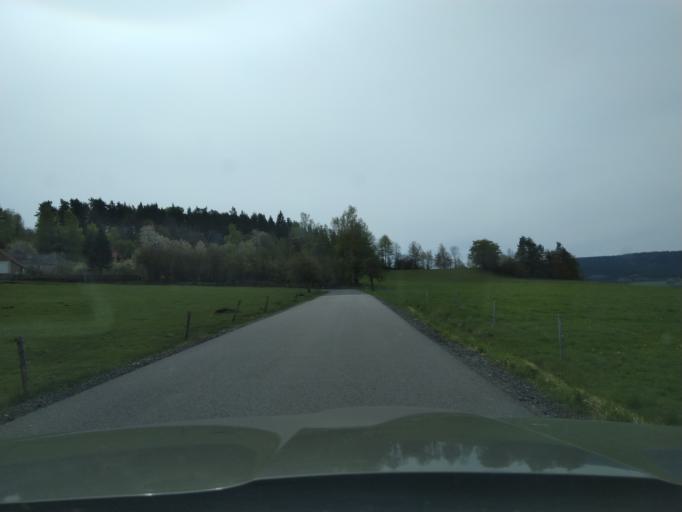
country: CZ
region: Jihocesky
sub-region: Okres Prachatice
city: Stachy
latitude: 49.1825
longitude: 13.6475
